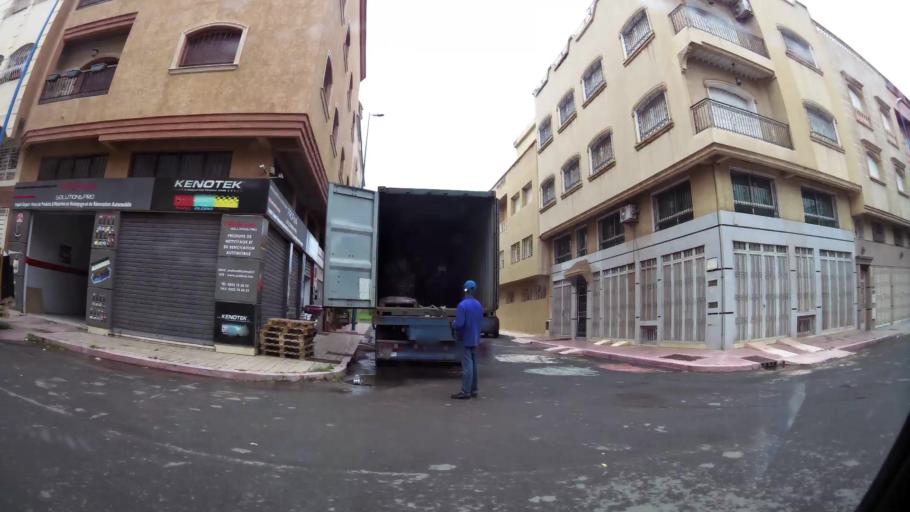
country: MA
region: Grand Casablanca
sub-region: Casablanca
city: Casablanca
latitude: 33.5391
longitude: -7.6508
